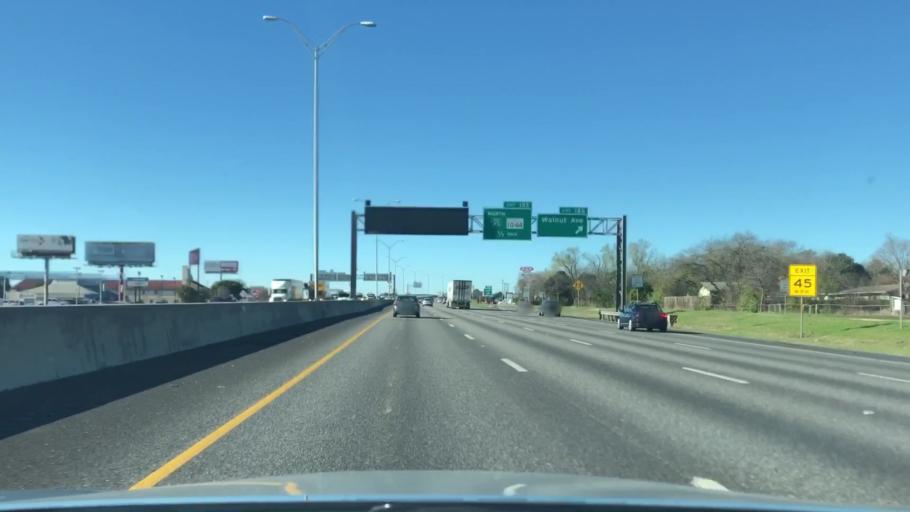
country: US
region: Texas
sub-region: Comal County
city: New Braunfels
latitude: 29.6884
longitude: -98.1193
